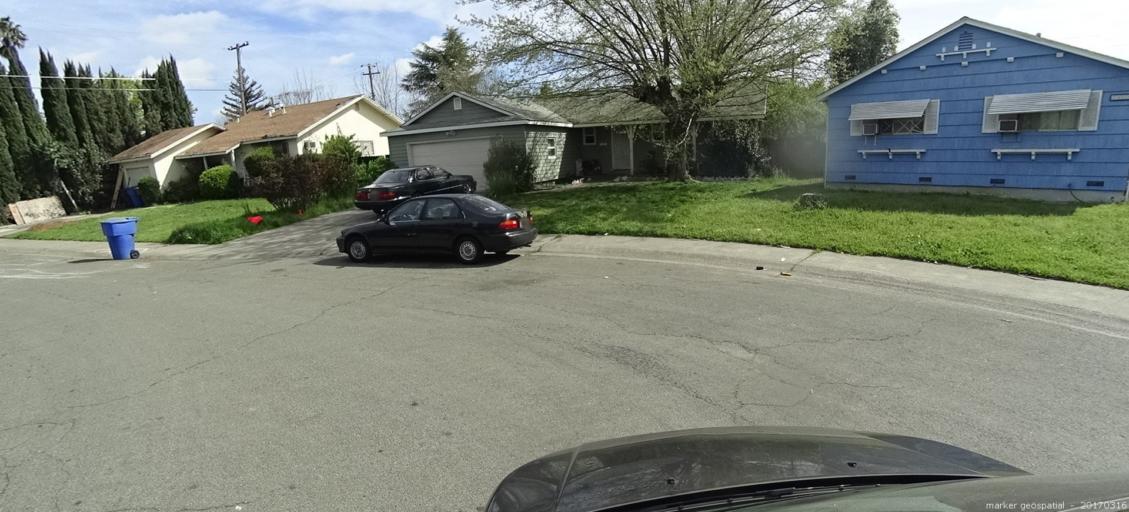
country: US
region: California
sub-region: Sacramento County
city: Parkway
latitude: 38.5051
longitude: -121.4882
